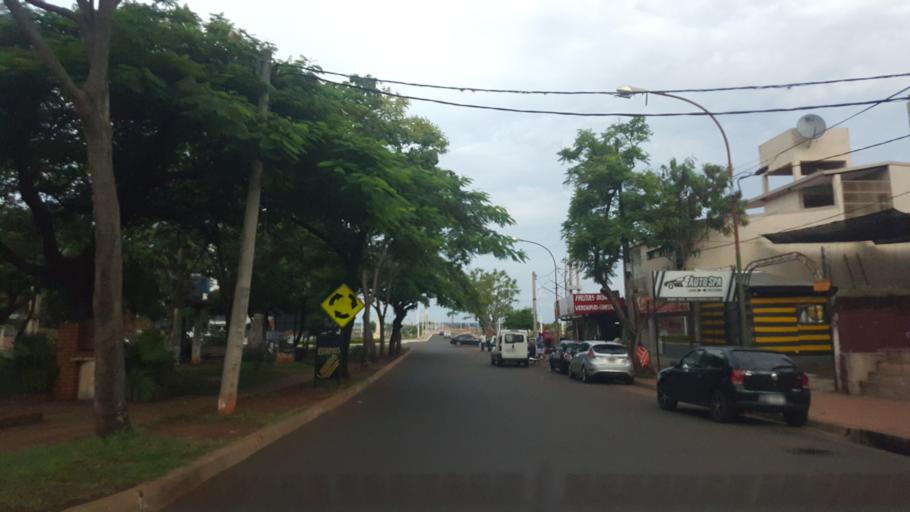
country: AR
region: Misiones
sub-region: Departamento de Capital
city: Posadas
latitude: -27.3754
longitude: -55.8892
